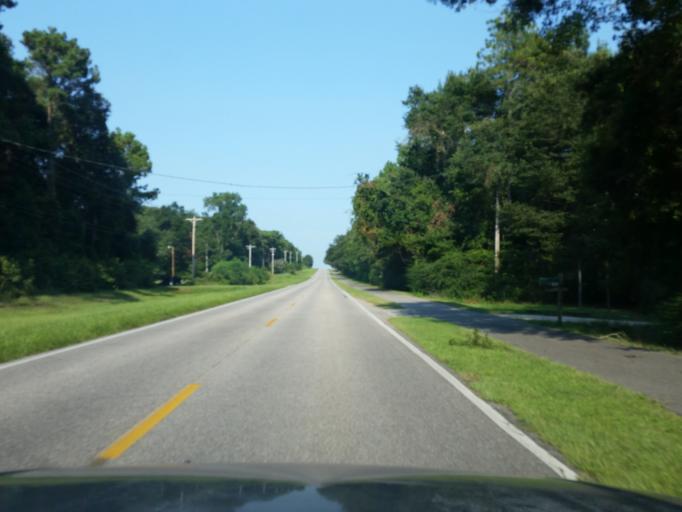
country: US
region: Alabama
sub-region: Baldwin County
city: Point Clear
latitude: 30.4211
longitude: -87.8997
